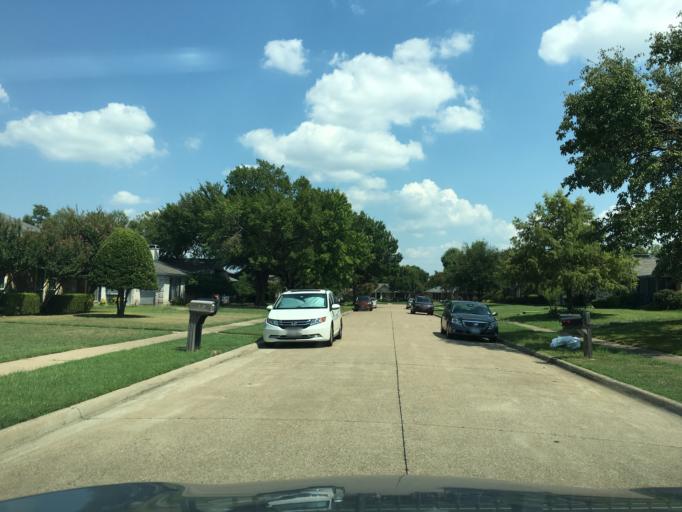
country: US
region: Texas
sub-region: Dallas County
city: Garland
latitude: 32.9501
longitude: -96.6637
